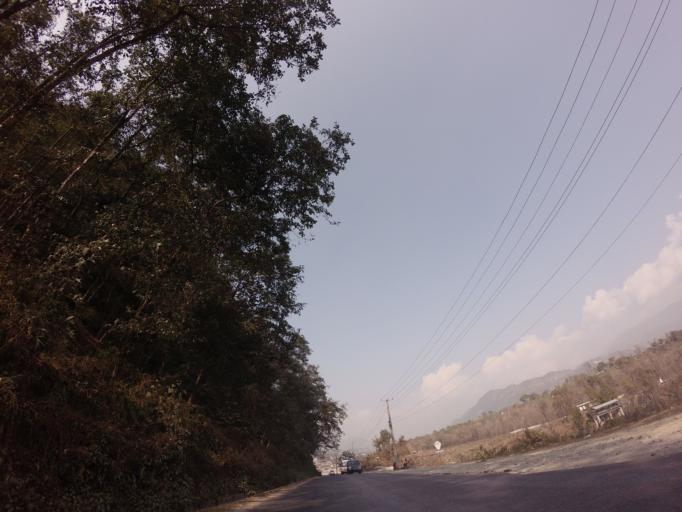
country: NP
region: Western Region
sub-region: Gandaki Zone
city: Pokhara
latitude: 28.2494
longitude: 83.9730
